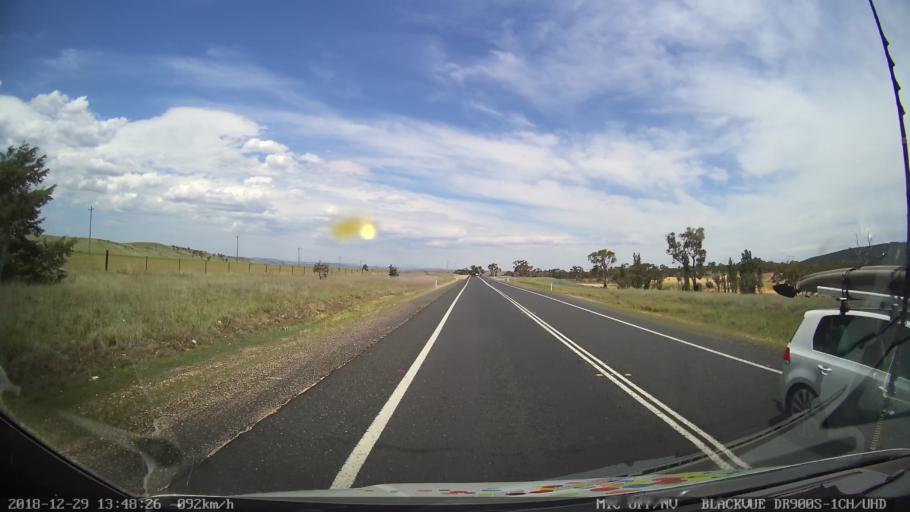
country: AU
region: New South Wales
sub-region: Cooma-Monaro
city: Cooma
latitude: -36.1401
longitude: 149.1479
